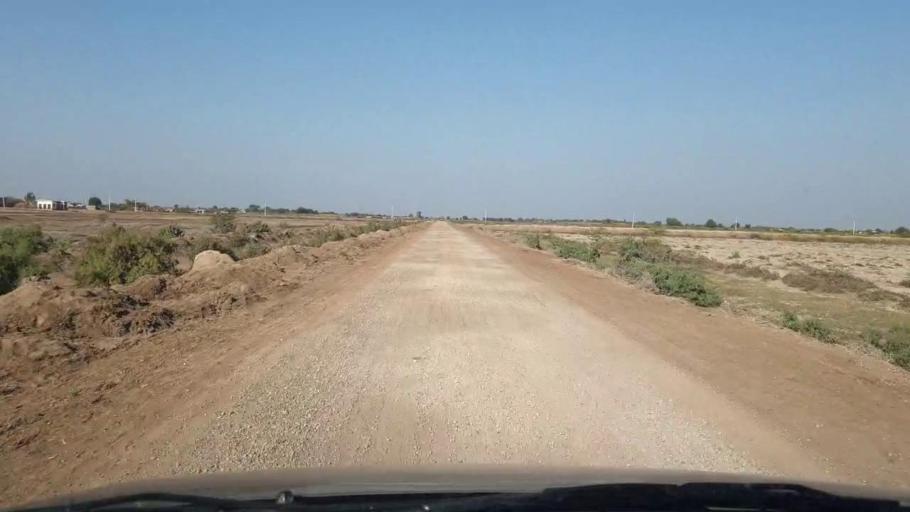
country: PK
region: Sindh
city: Digri
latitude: 25.1362
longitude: 69.2790
